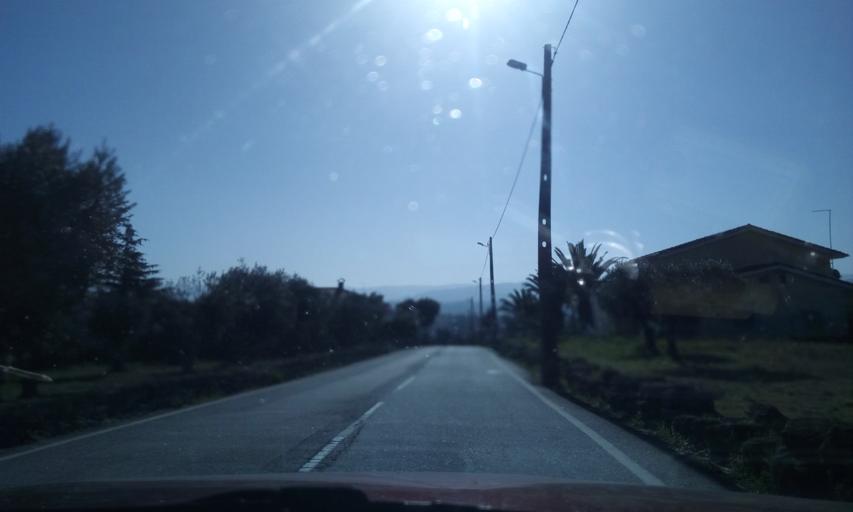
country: PT
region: Guarda
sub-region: Celorico da Beira
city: Celorico da Beira
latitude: 40.6722
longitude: -7.3953
